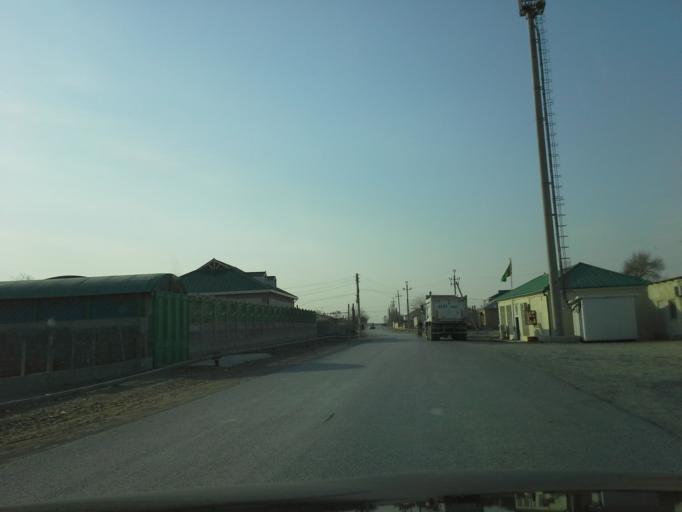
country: TM
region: Ahal
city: Abadan
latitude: 38.1734
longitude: 58.0441
